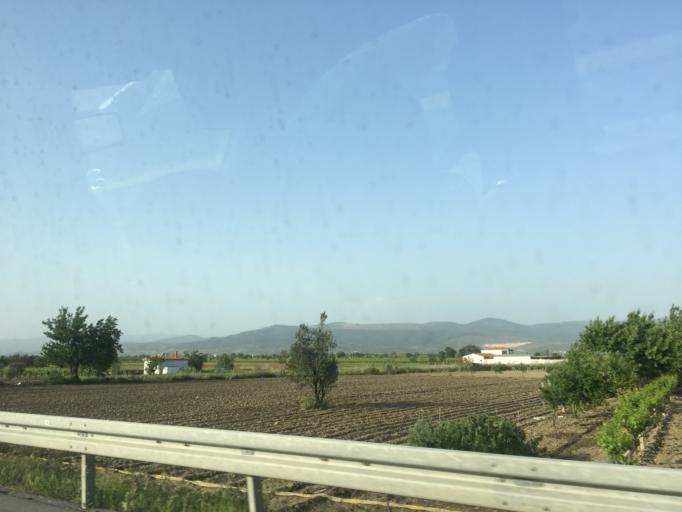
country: TR
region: Manisa
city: Golmarmara
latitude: 38.6823
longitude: 27.9424
